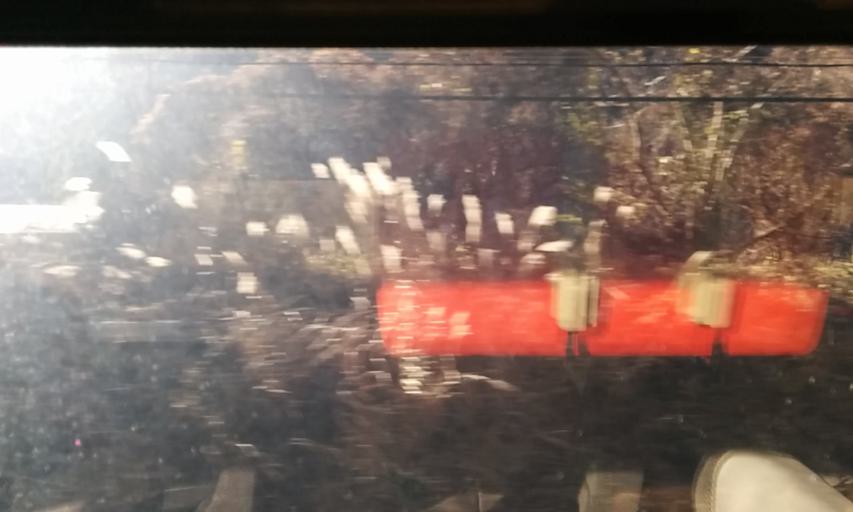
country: JP
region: Nagano
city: Ina
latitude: 35.7569
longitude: 137.7100
